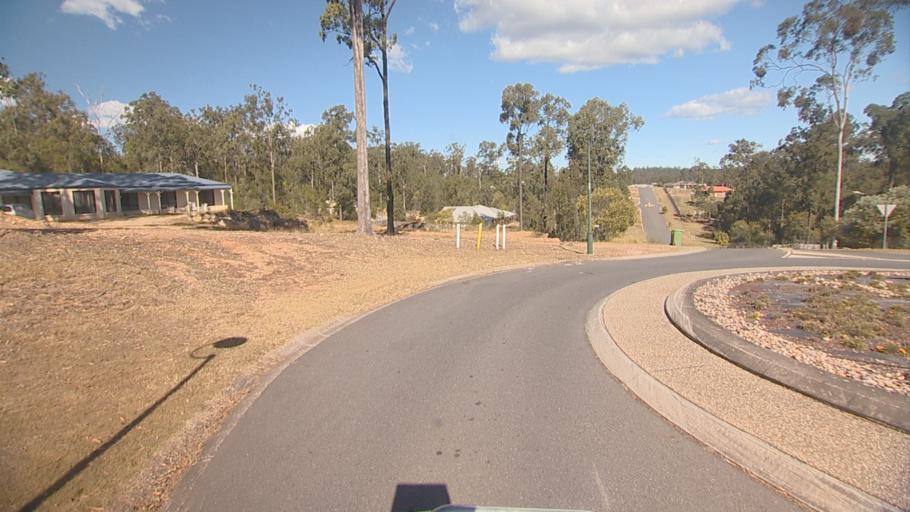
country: AU
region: Queensland
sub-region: Logan
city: North Maclean
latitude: -27.7551
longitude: 152.9362
